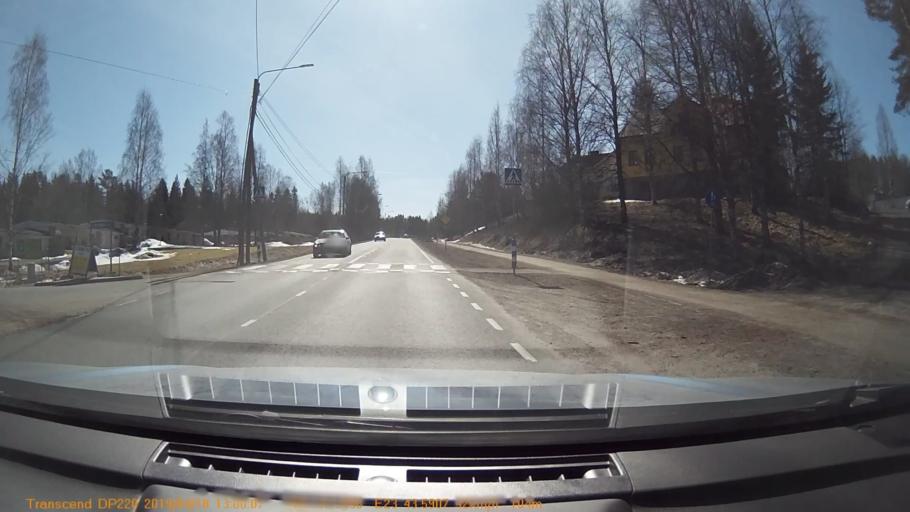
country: FI
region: Pirkanmaa
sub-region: Tampere
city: Kuru
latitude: 61.8725
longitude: 23.7263
